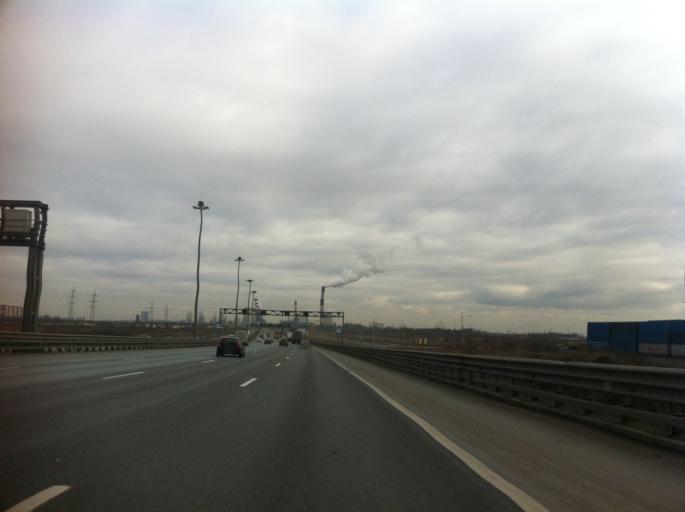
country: RU
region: St.-Petersburg
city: Shushary
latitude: 59.8187
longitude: 30.4057
